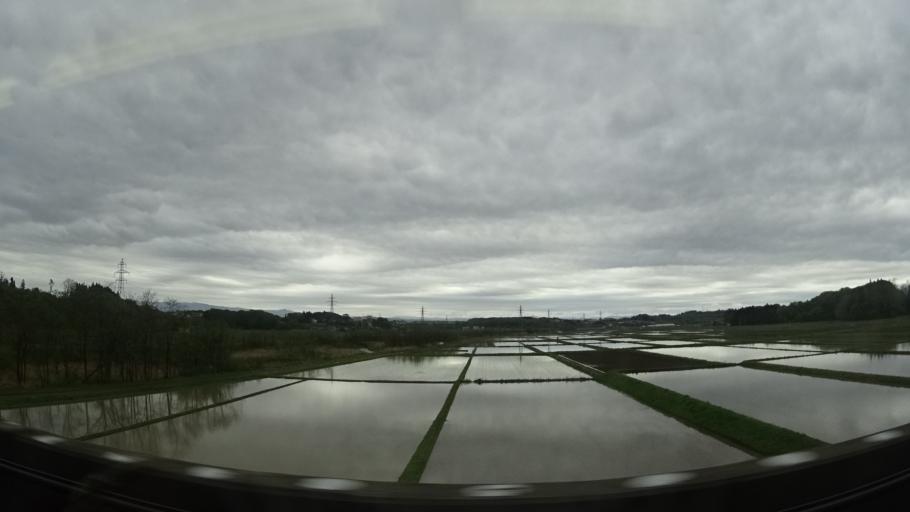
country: JP
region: Fukushima
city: Sukagawa
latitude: 37.2608
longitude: 140.3099
